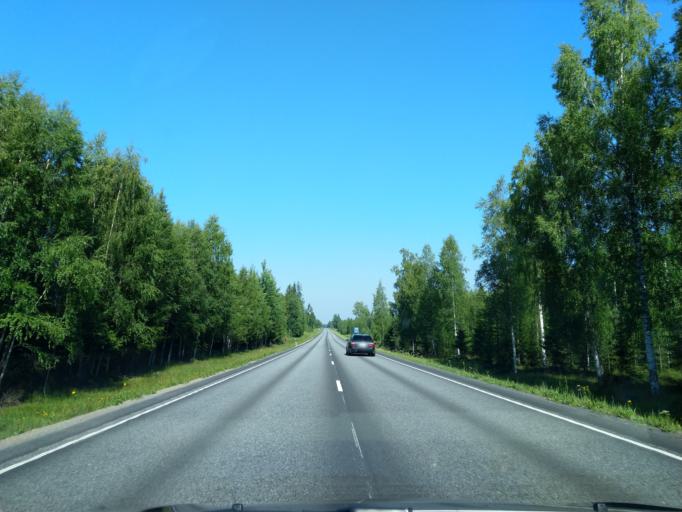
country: FI
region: Satakunta
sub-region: Pori
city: Huittinen
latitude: 61.1304
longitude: 22.7910
